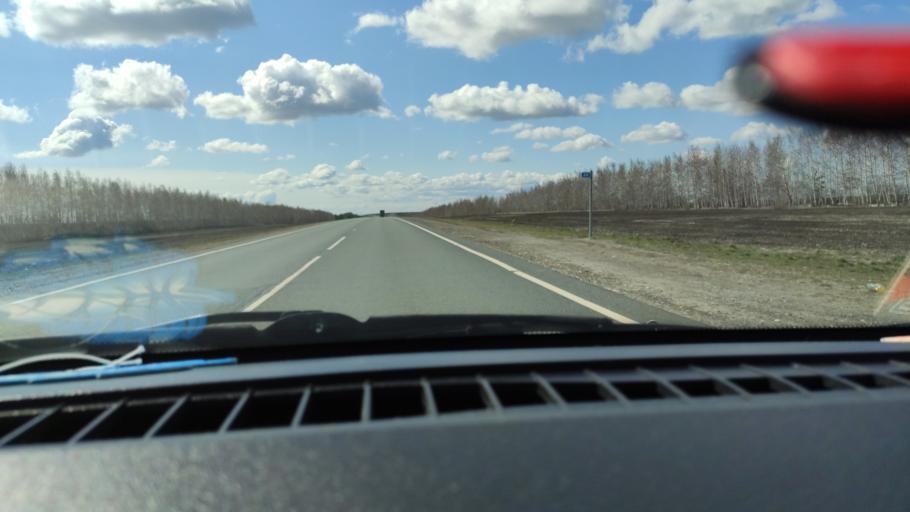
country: RU
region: Samara
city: Syzran'
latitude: 52.9049
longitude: 48.2976
